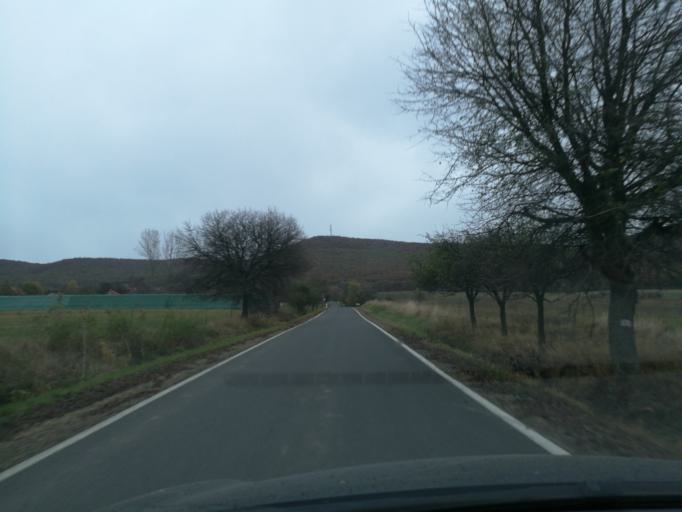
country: HU
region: Nograd
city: Paszto
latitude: 47.9773
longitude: 19.6335
